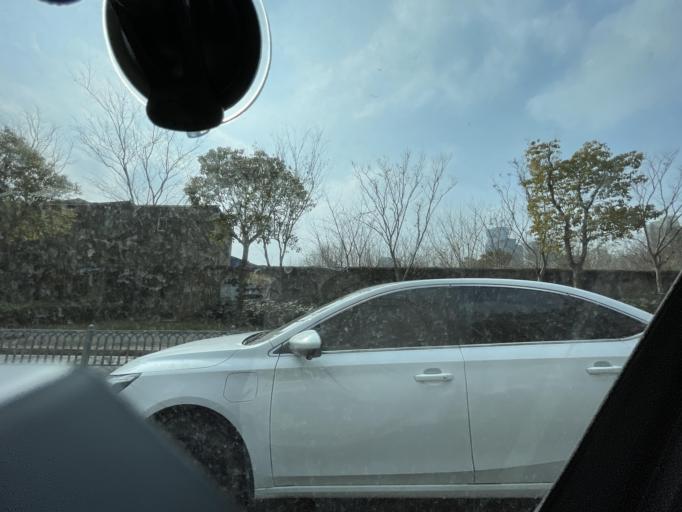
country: CN
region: Shanghai Shi
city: Yangpu
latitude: 31.3188
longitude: 121.5121
